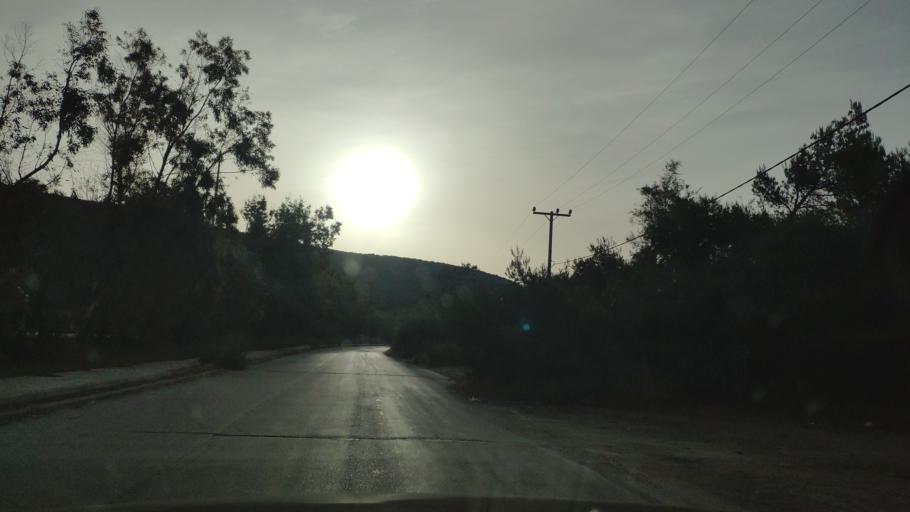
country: GR
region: Attica
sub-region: Nomarchia Anatolikis Attikis
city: Limin Mesoyaias
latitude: 37.8674
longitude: 24.0345
